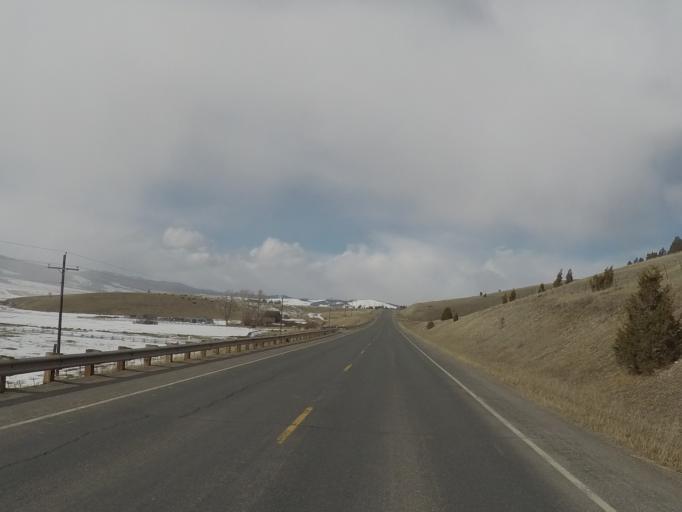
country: US
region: Montana
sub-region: Granite County
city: Philipsburg
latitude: 46.2847
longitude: -113.3225
